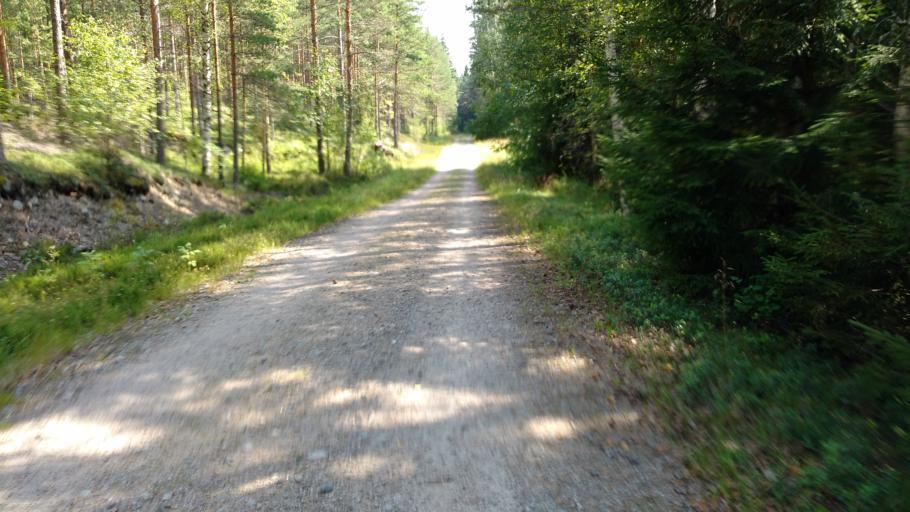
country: FI
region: Varsinais-Suomi
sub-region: Salo
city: Pertteli
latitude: 60.4030
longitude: 23.2126
